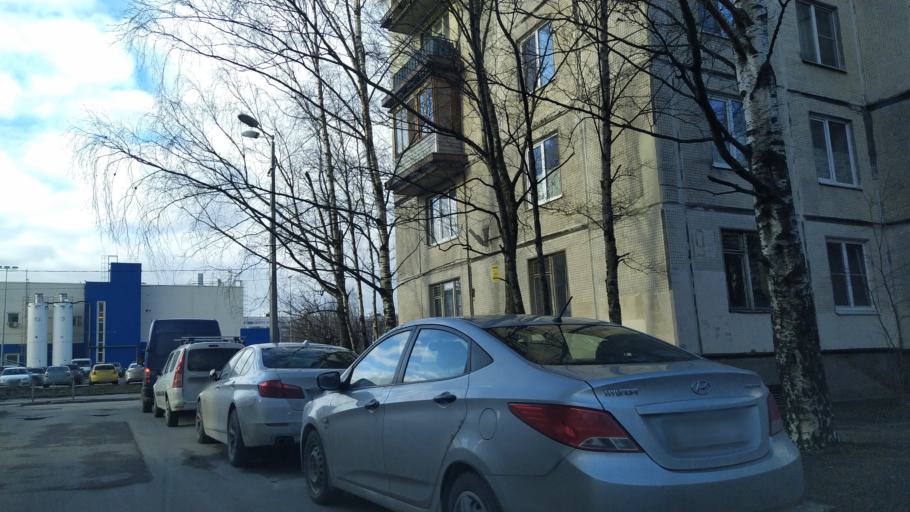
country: RU
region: Leningrad
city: Parnas
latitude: 60.0469
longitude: 30.3682
